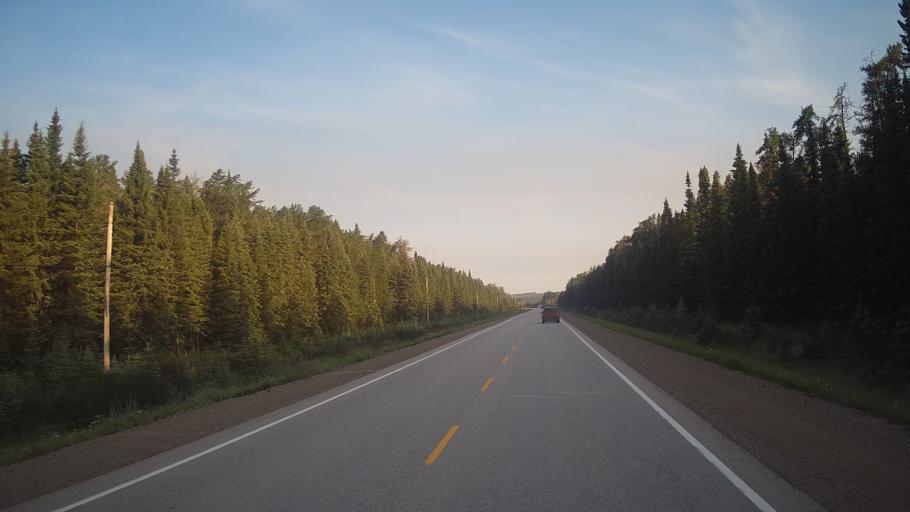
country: CA
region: Ontario
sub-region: Rainy River District
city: Atikokan
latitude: 49.2462
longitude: -91.0955
